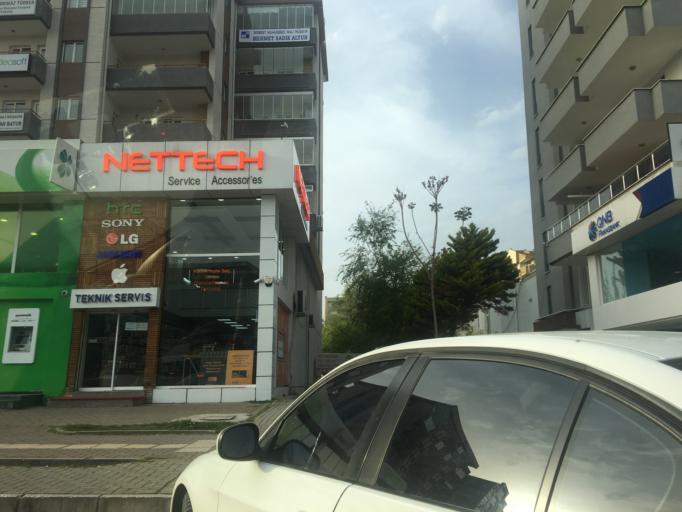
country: TR
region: Bursa
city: Yildirim
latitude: 40.2119
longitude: 28.9831
